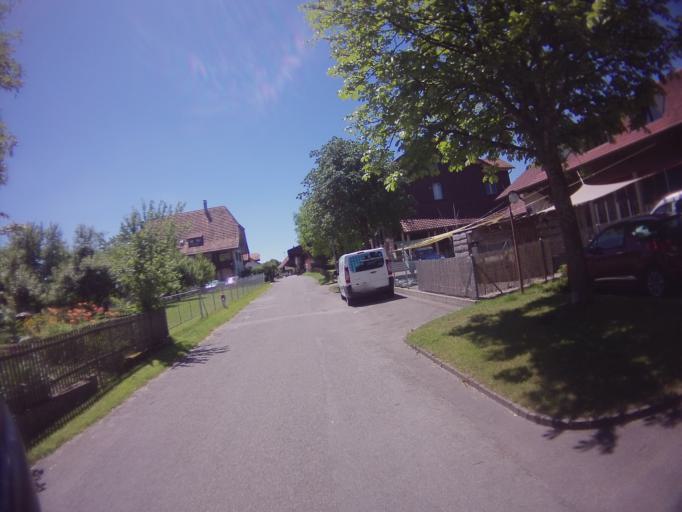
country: CH
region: Bern
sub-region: Bern-Mittelland District
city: Jegenstorf
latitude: 47.0456
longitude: 7.5220
